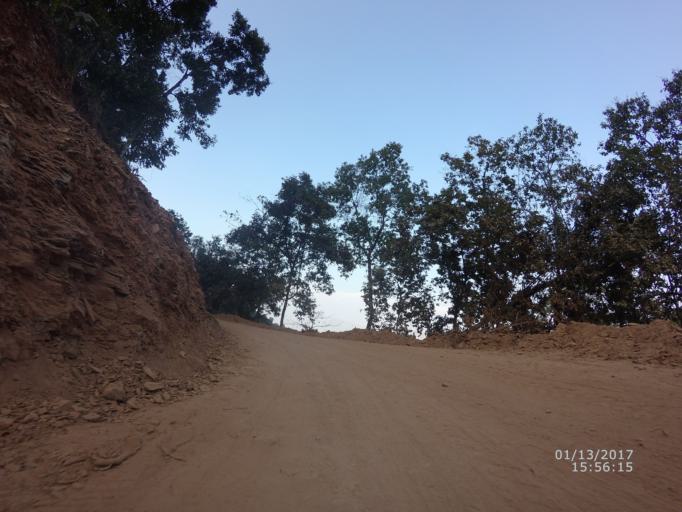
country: NP
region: Western Region
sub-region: Gandaki Zone
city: Pokhara
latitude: 28.1581
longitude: 84.0027
